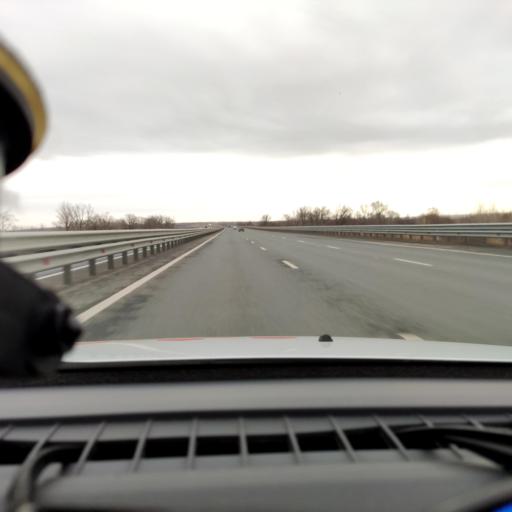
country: RU
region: Samara
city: Smyshlyayevka
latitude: 53.1722
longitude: 50.3136
